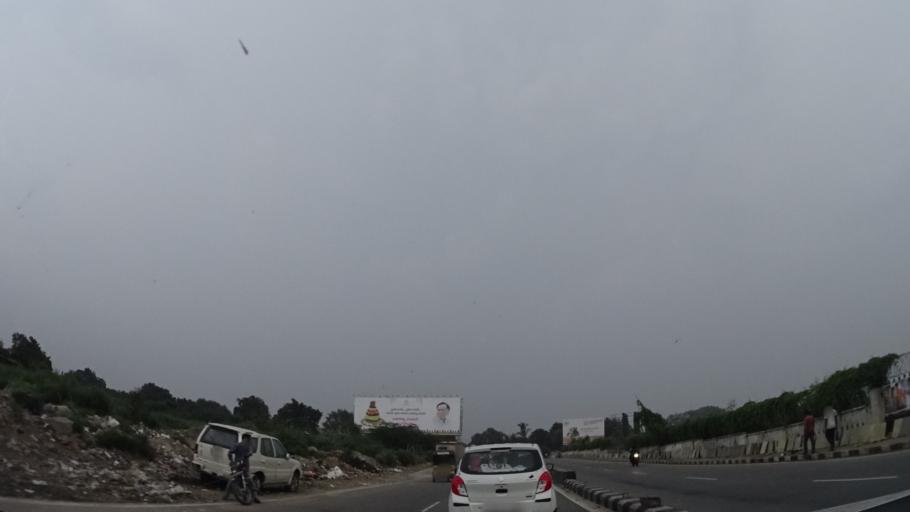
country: IN
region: Telangana
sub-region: Hyderabad
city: Malkajgiri
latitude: 17.4535
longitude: 78.4859
